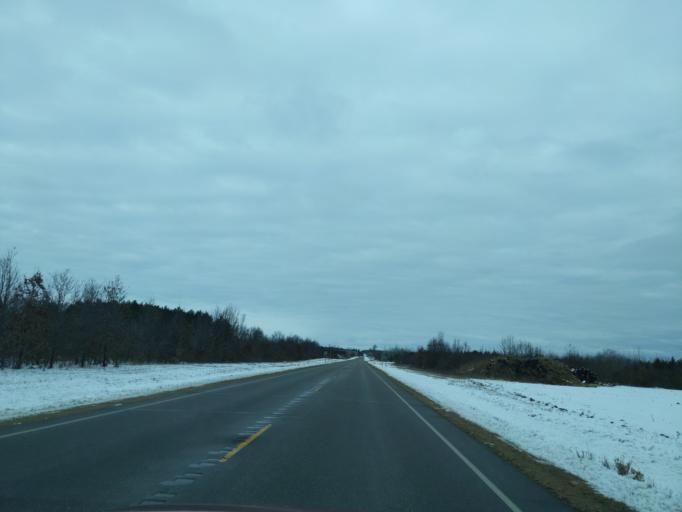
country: US
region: Wisconsin
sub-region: Waushara County
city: Wautoma
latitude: 43.9795
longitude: -89.3276
